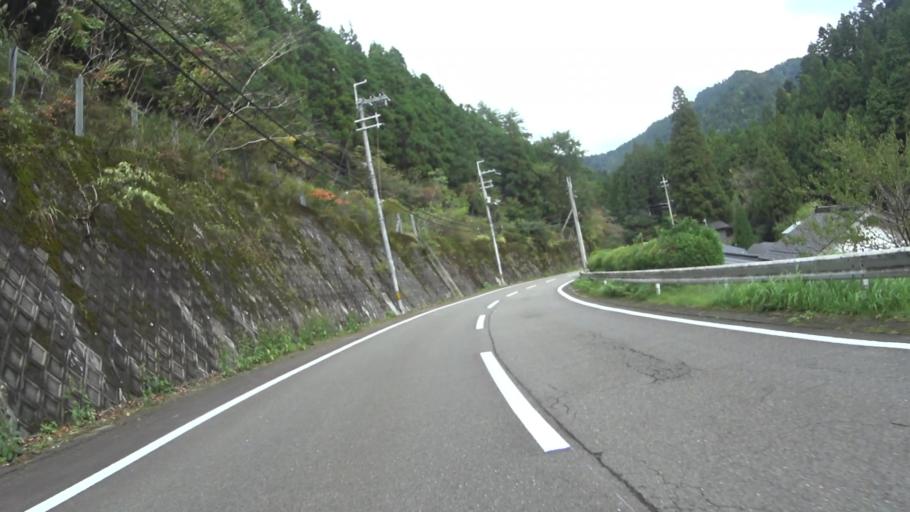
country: JP
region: Shiga Prefecture
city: Kitahama
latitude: 35.2168
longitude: 135.7774
